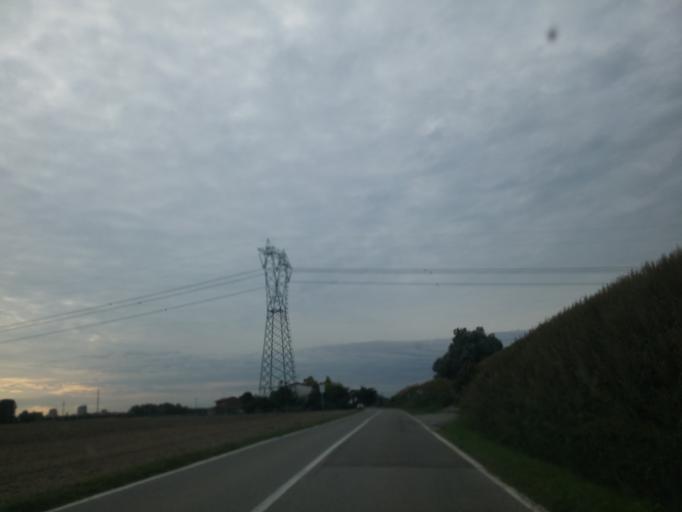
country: IT
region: Emilia-Romagna
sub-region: Provincia di Bologna
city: Longara
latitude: 44.5890
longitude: 11.3200
